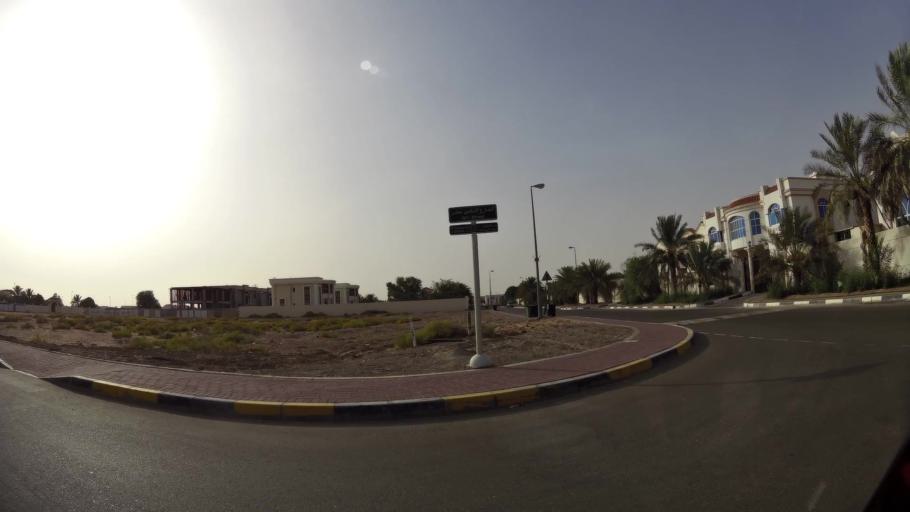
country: AE
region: Abu Dhabi
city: Al Ain
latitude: 24.2233
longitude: 55.6614
